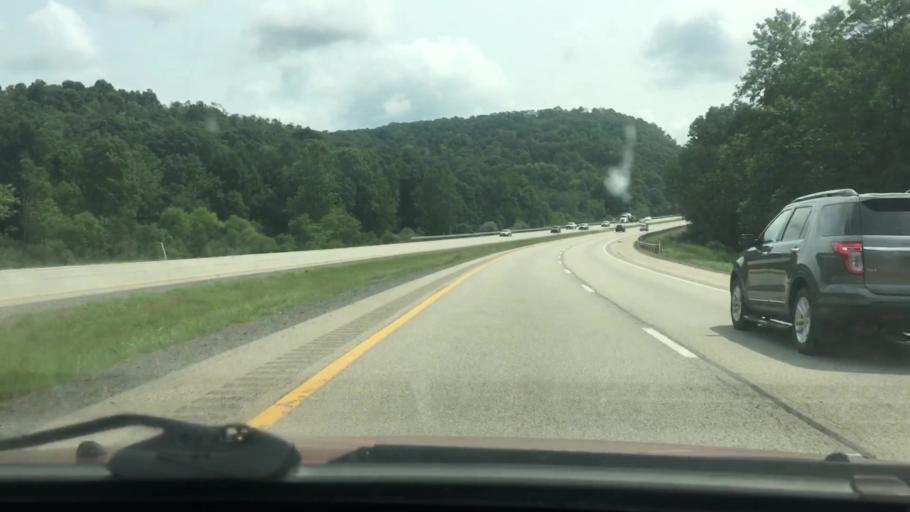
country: US
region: West Virginia
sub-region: Monongalia County
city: Cheat Lake
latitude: 39.6503
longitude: -79.7154
